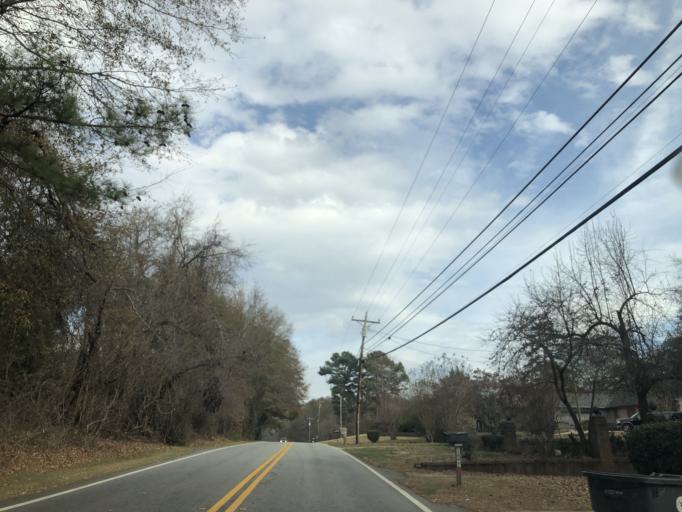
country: US
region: Georgia
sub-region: Henry County
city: Stockbridge
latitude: 33.6258
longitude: -84.2277
